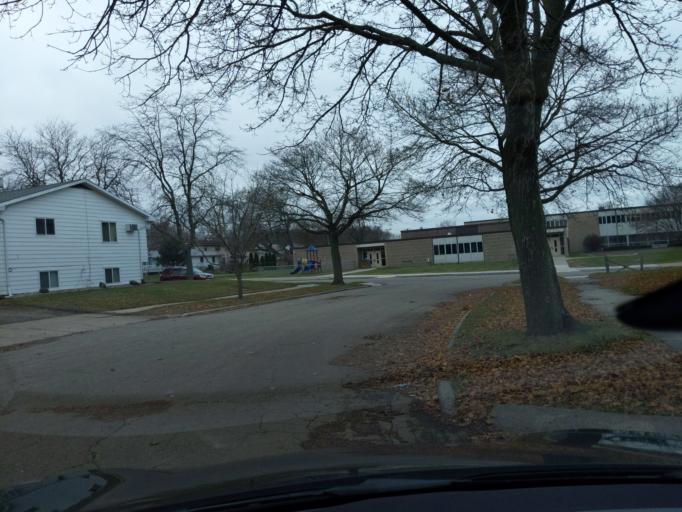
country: US
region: Michigan
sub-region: Ingham County
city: Lansing
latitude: 42.7061
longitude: -84.5830
